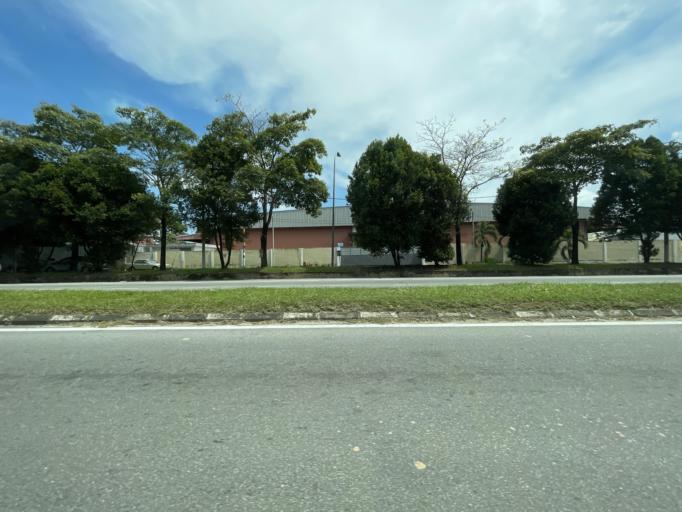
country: MY
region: Melaka
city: Batu Berendam
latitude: 2.2866
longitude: 102.2419
